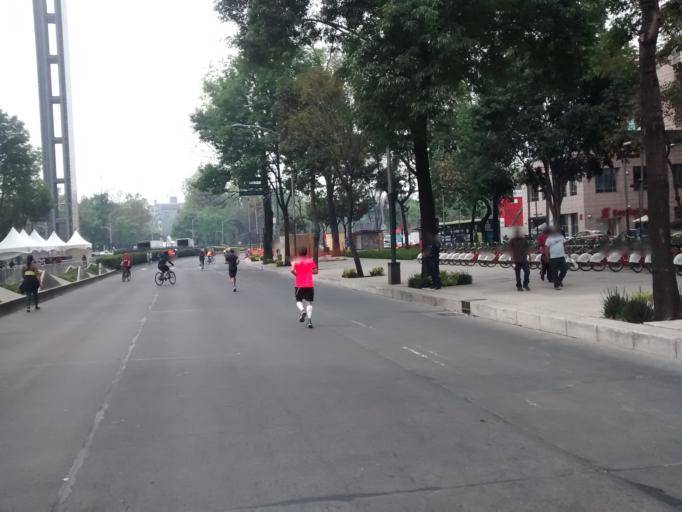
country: MX
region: Mexico City
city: Polanco
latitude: 19.4238
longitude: -99.1746
